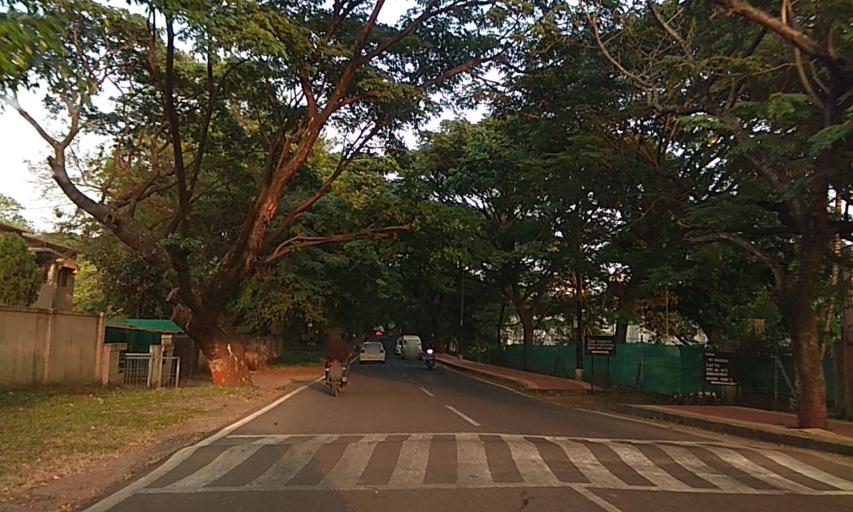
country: IN
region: Maharashtra
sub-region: Pune Division
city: Khadki
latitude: 18.5568
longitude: 73.8554
